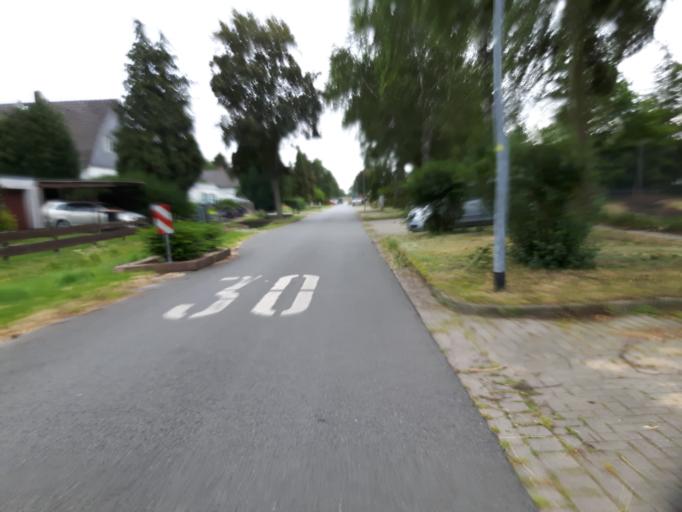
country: DE
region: Lower Saxony
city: Winsen
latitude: 53.3800
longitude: 10.1949
